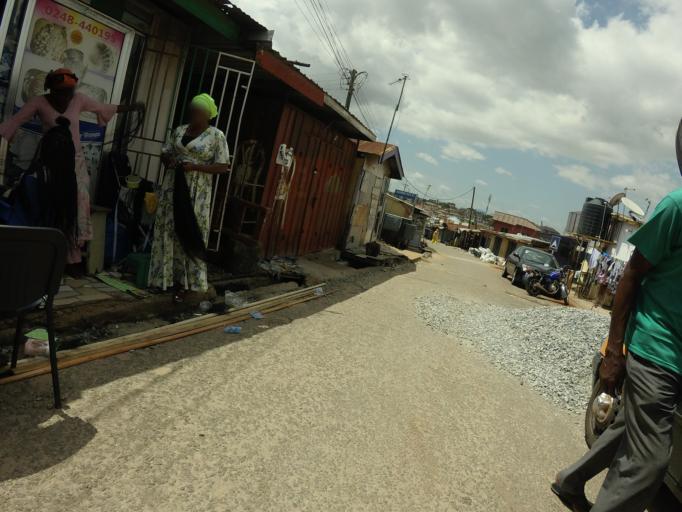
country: GH
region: Greater Accra
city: Accra
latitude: 5.5840
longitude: -0.2002
